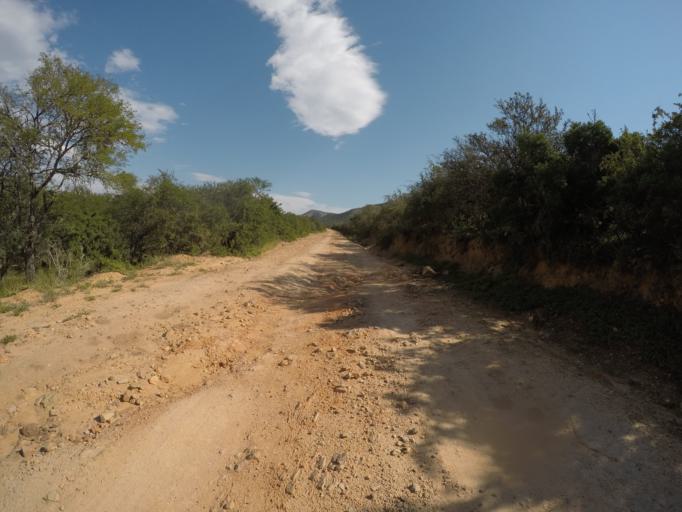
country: ZA
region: Eastern Cape
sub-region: Cacadu District Municipality
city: Kareedouw
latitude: -33.6548
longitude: 24.4169
